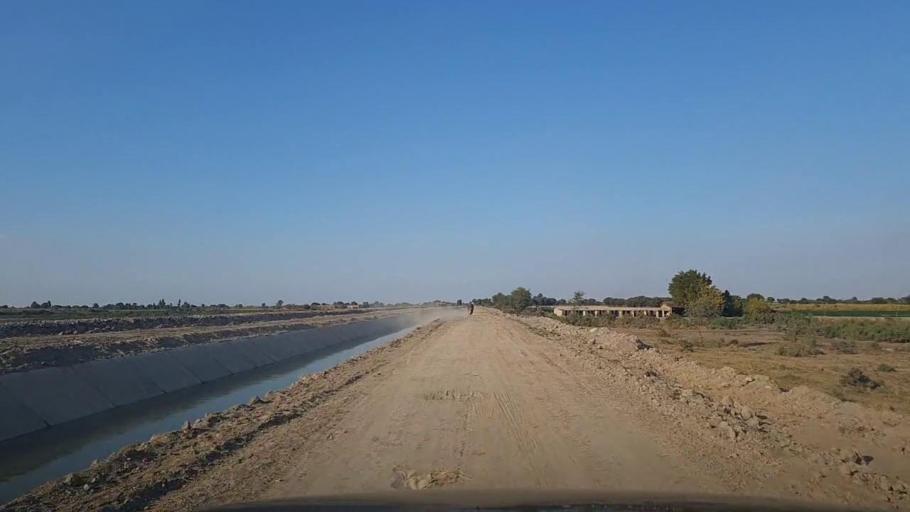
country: PK
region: Sindh
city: Jhol
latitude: 25.8893
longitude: 69.0380
